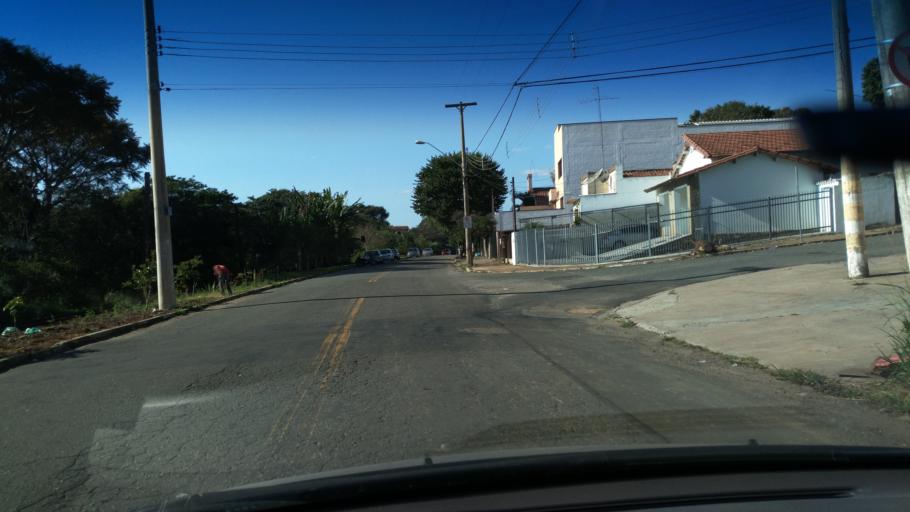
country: BR
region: Sao Paulo
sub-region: Valinhos
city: Valinhos
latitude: -22.9639
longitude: -46.9928
